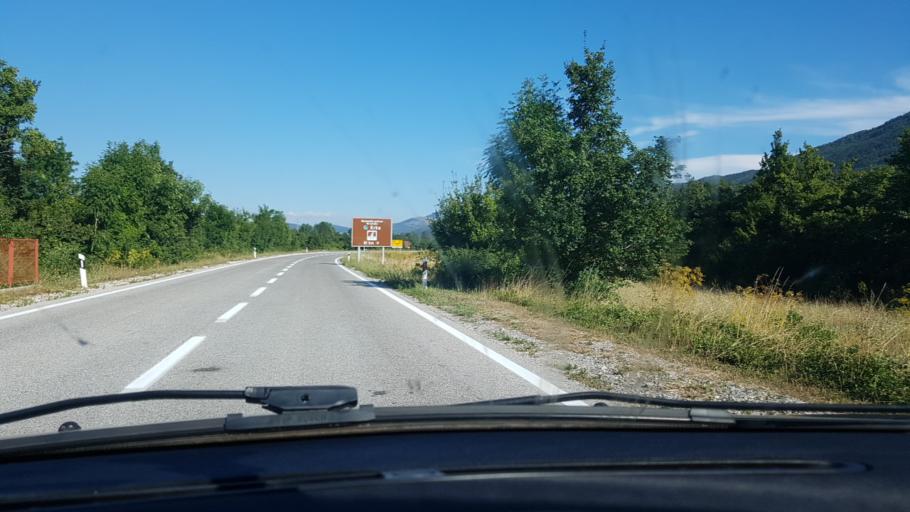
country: HR
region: Zadarska
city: Gracac
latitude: 44.2976
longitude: 15.8338
